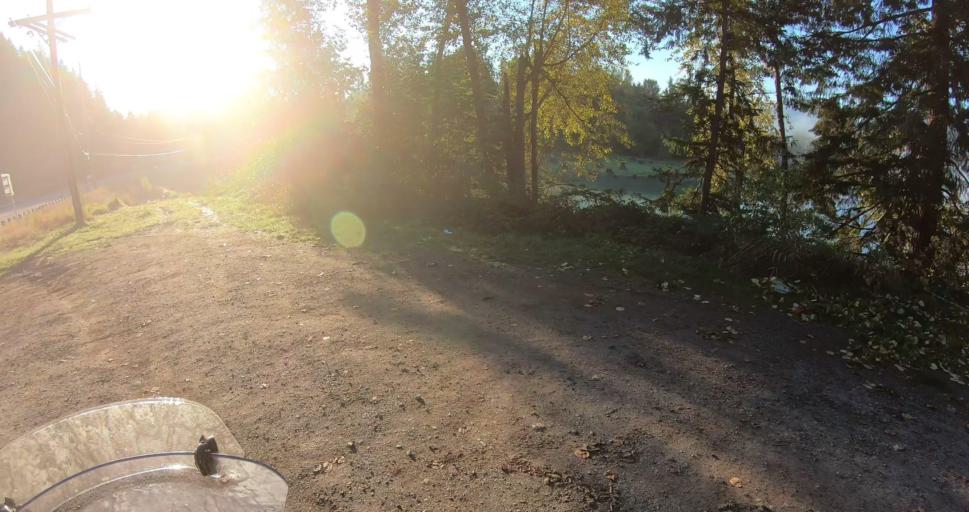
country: US
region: Washington
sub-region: Pierce County
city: Eatonville
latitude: 46.7959
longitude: -122.2774
